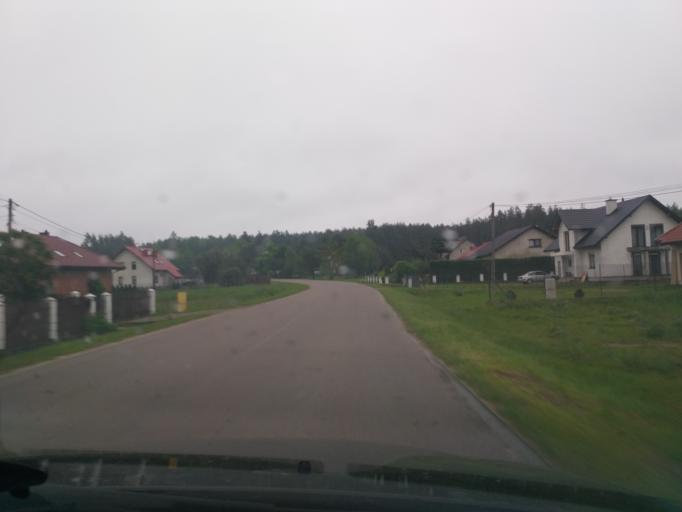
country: PL
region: Subcarpathian Voivodeship
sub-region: Powiat debicki
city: Pilzno
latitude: 49.9763
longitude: 21.3486
